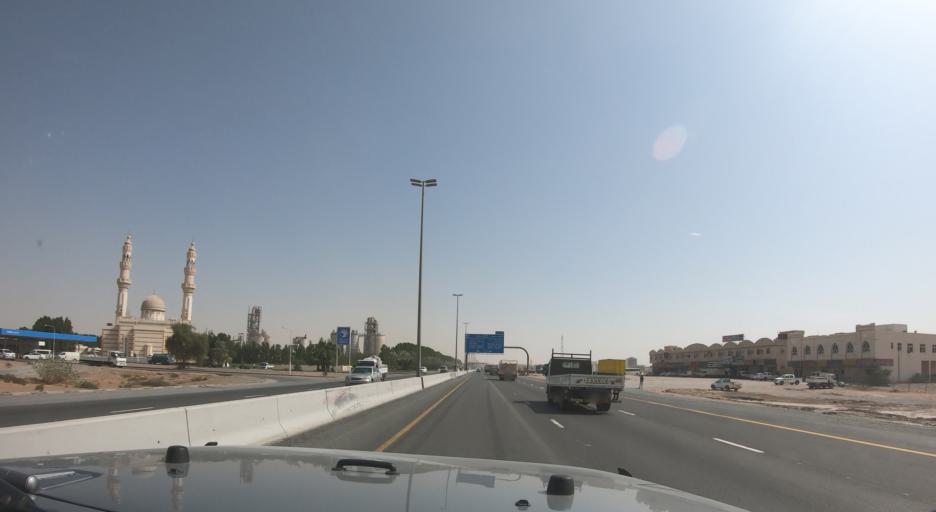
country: AE
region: Ash Shariqah
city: Sharjah
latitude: 25.2962
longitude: 55.6090
